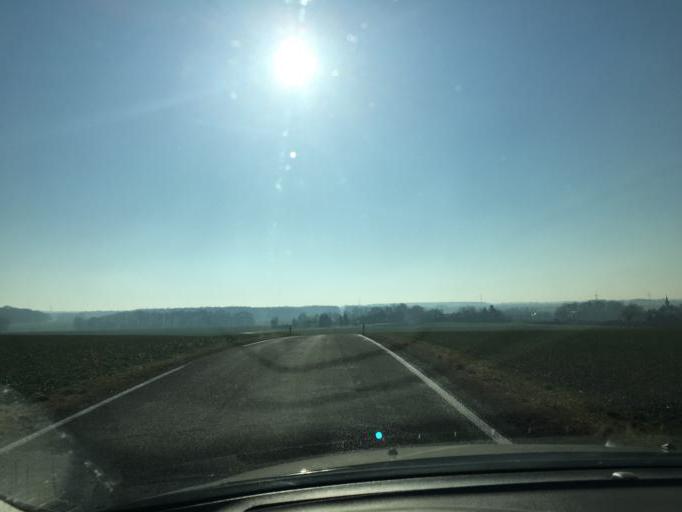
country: DE
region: Saxony
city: Bad Lausick
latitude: 51.1110
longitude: 12.6616
